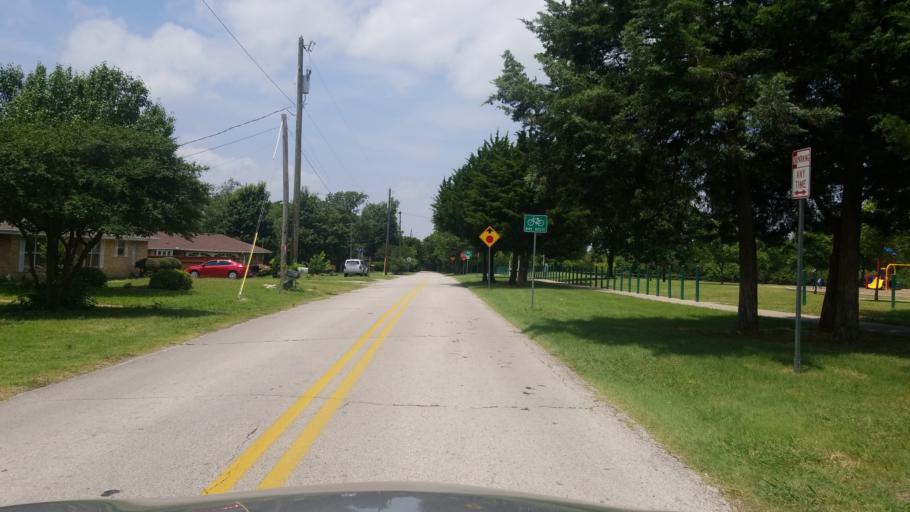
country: US
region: Texas
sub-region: Dallas County
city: Duncanville
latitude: 32.6746
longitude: -96.9134
